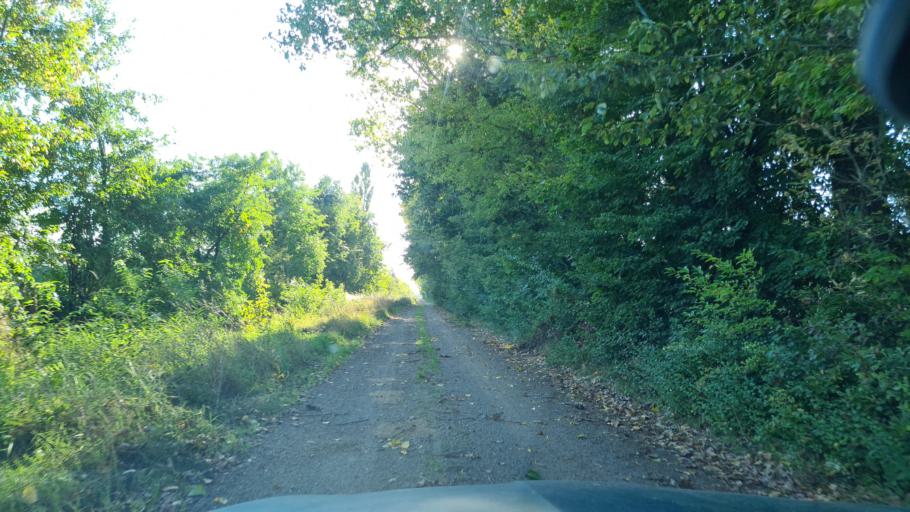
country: DE
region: Brandenburg
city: Bad Liebenwerda
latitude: 51.5251
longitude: 13.3504
